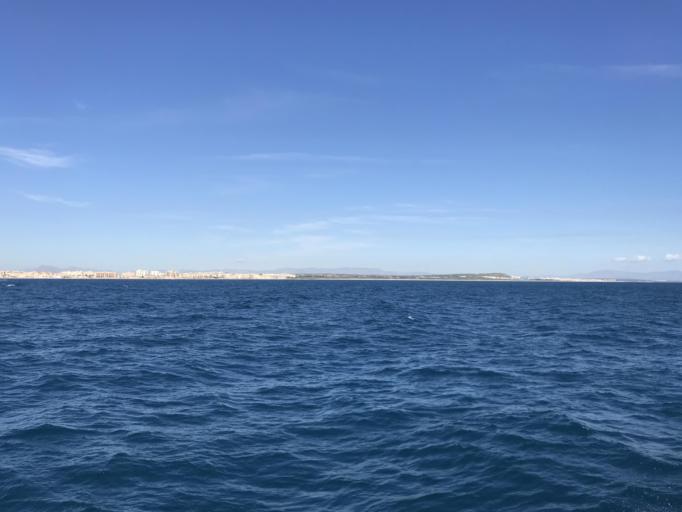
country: ES
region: Valencia
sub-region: Provincia de Alicante
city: Torrevieja
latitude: 38.0091
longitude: -0.6306
